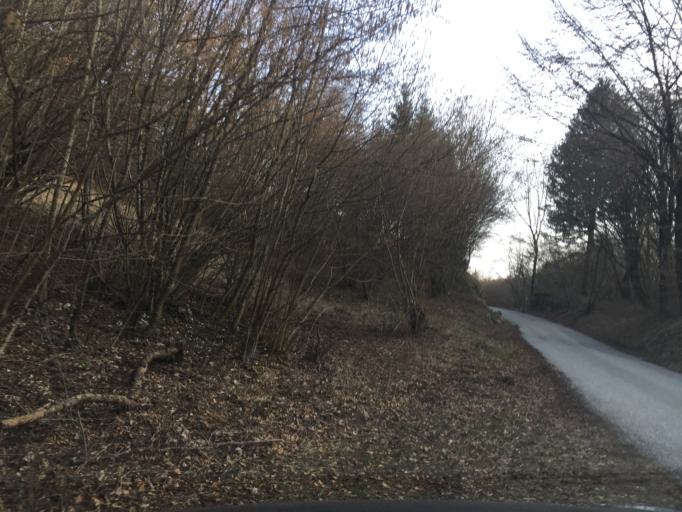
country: SI
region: Kanal
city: Kanal
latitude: 46.0560
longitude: 13.6661
